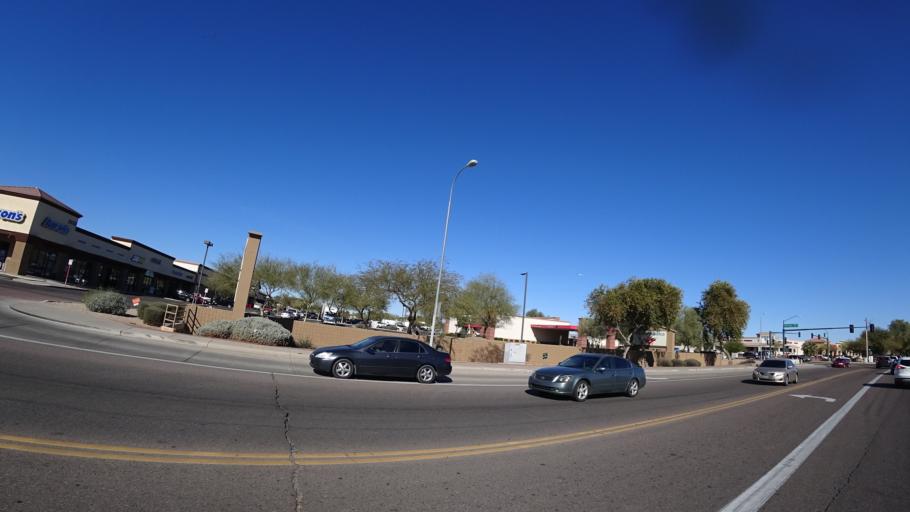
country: US
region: Arizona
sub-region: Maricopa County
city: Tolleson
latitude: 33.4229
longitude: -112.2397
